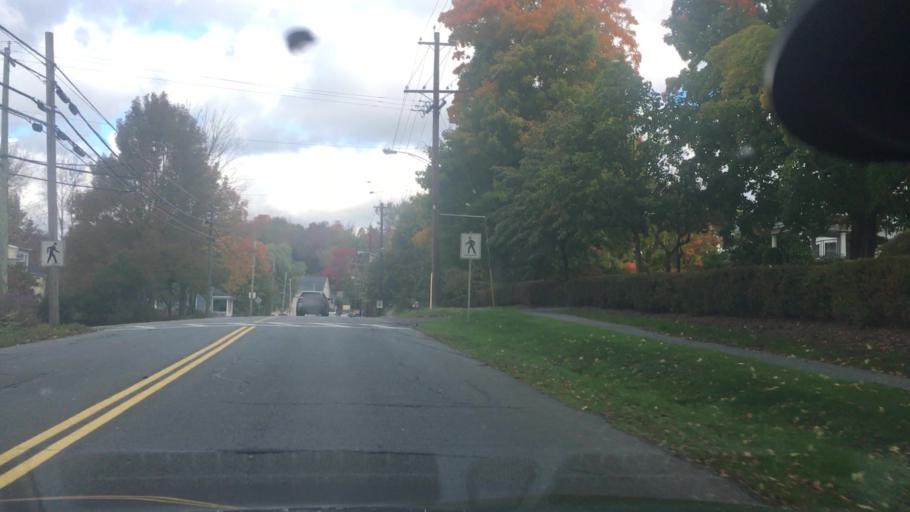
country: CA
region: Nova Scotia
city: Windsor
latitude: 44.9837
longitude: -64.1307
